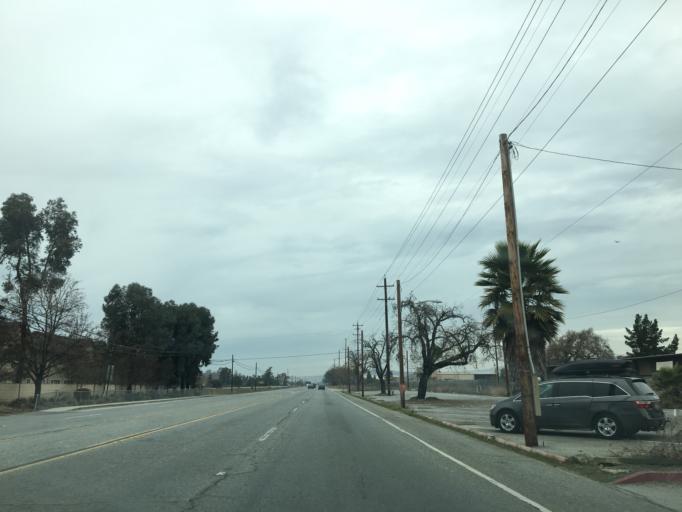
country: US
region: California
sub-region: Santa Clara County
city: San Martin
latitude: 37.0871
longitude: -121.6115
